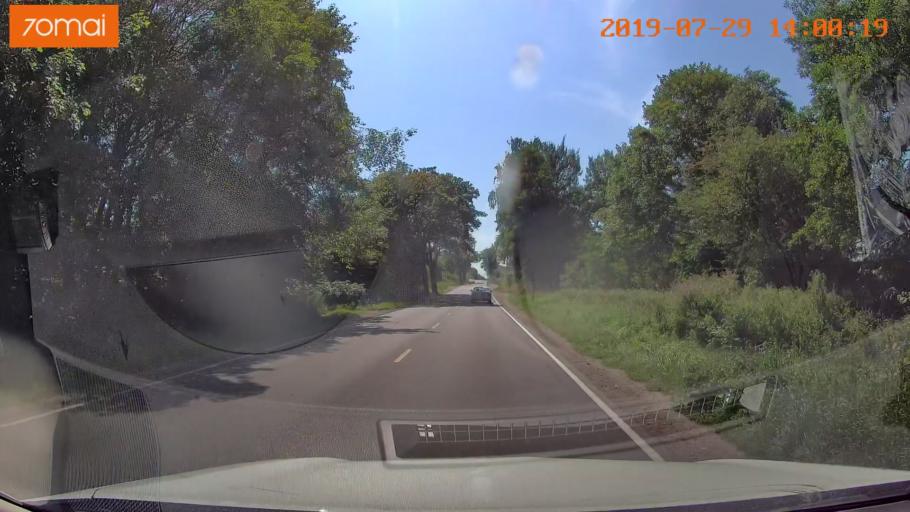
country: RU
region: Kaliningrad
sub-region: Gorod Kaliningrad
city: Baltiysk
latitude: 54.6796
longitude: 19.9287
